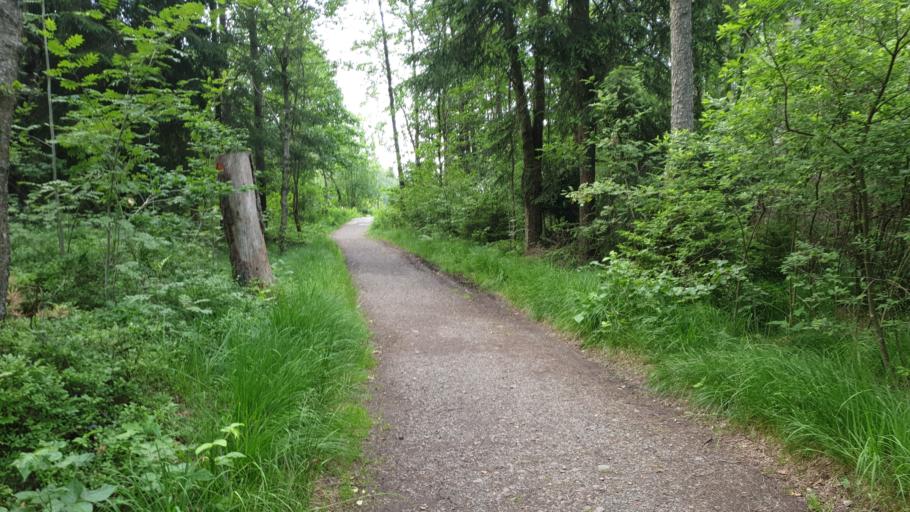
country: SE
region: Vaestra Goetaland
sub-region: Molndal
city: Moelndal
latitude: 57.6683
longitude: 12.0420
